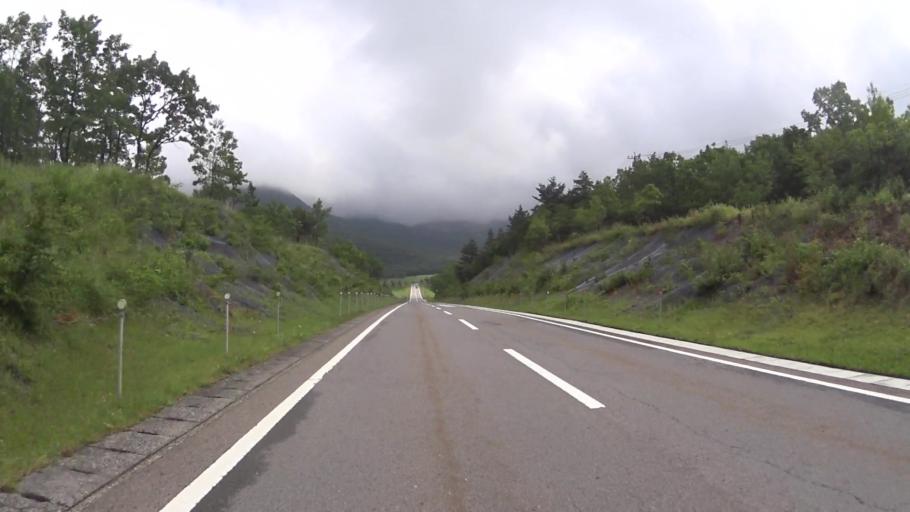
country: JP
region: Oita
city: Tsukawaki
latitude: 33.1259
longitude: 131.2290
